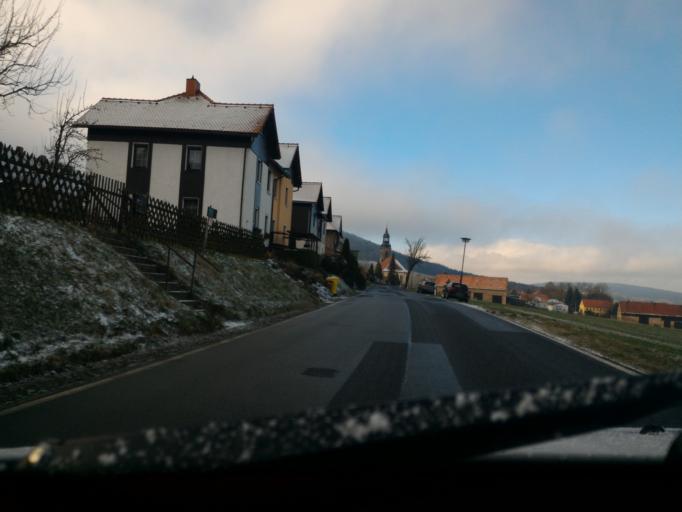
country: DE
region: Saxony
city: Grossschonau
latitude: 50.8688
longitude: 14.6557
